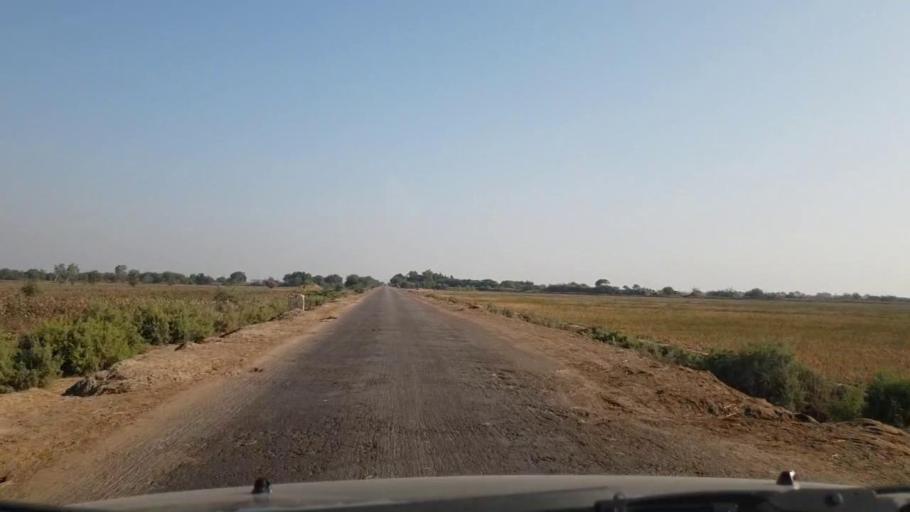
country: PK
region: Sindh
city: Tando Bago
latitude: 24.8583
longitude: 69.0441
